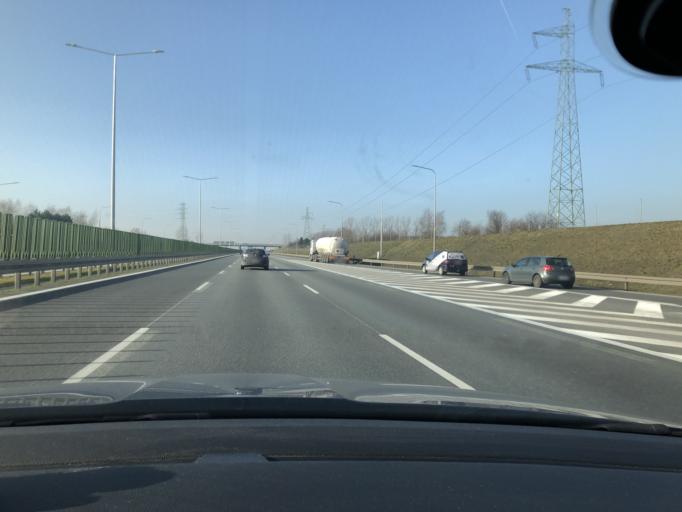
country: PL
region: Greater Poland Voivodeship
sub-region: Powiat poznanski
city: Komorniki
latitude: 52.3504
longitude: 16.8298
